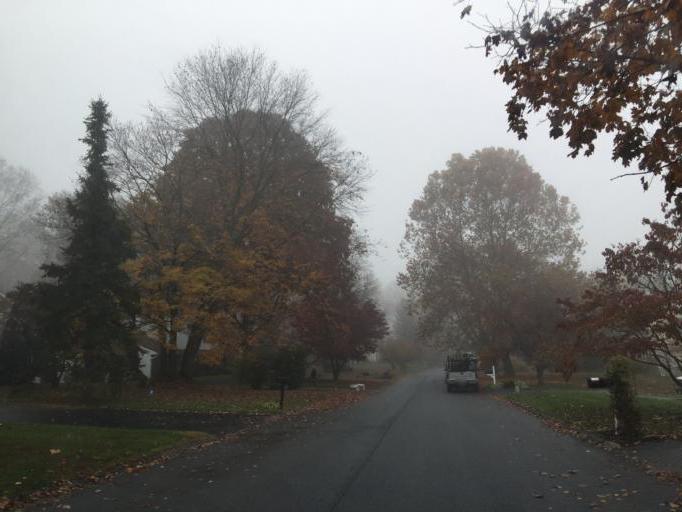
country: US
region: Maryland
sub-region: Howard County
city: Columbia
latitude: 39.2606
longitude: -76.8533
